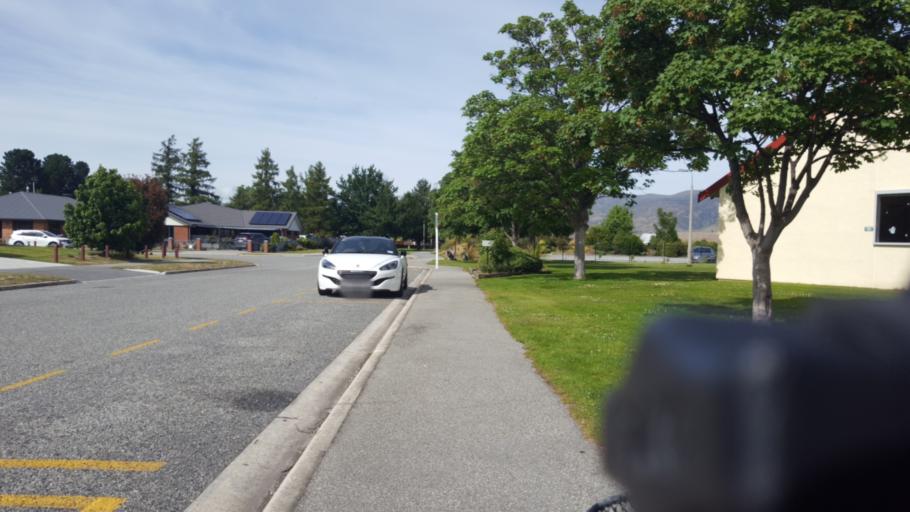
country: NZ
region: Otago
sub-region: Queenstown-Lakes District
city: Wanaka
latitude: -45.0431
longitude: 169.1869
